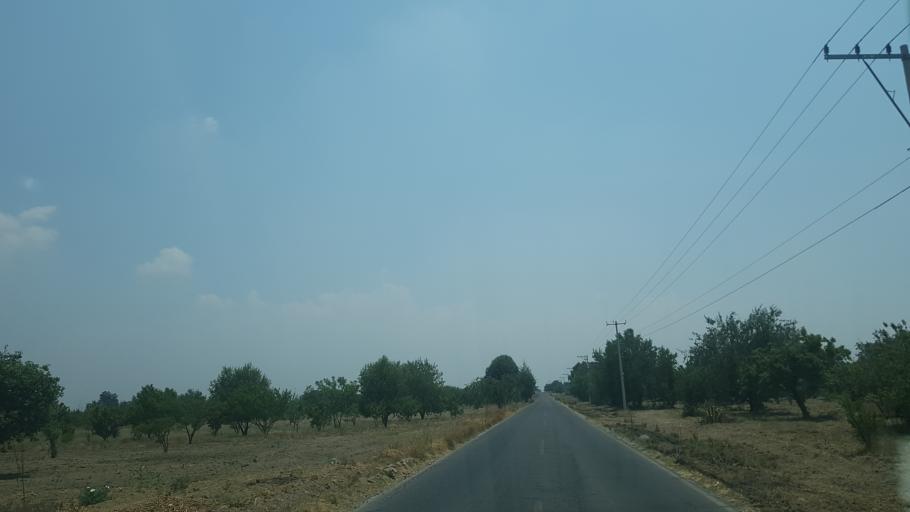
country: MX
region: Puebla
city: San Andres Calpan
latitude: 19.0989
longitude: -98.4287
